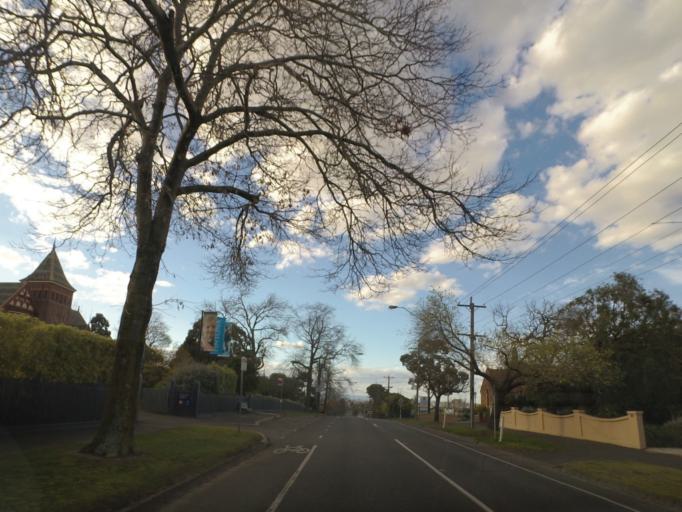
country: AU
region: Victoria
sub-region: Boroondara
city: Canterbury
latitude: -37.8152
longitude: 145.0808
